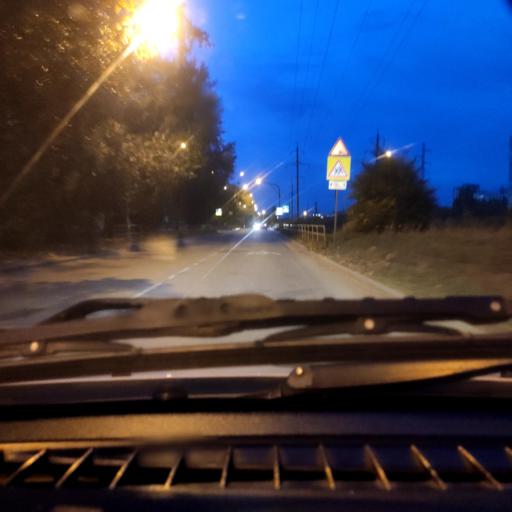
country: RU
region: Samara
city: Zhigulevsk
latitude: 53.4717
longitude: 49.5168
